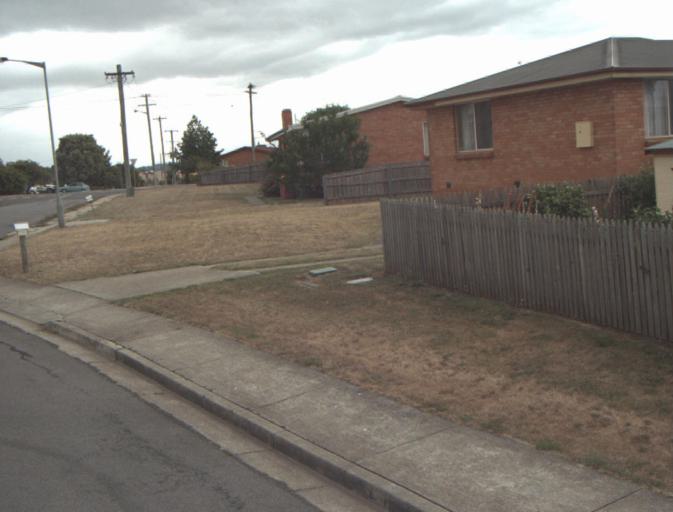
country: AU
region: Tasmania
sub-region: Launceston
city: Newstead
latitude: -41.4369
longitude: 147.1911
